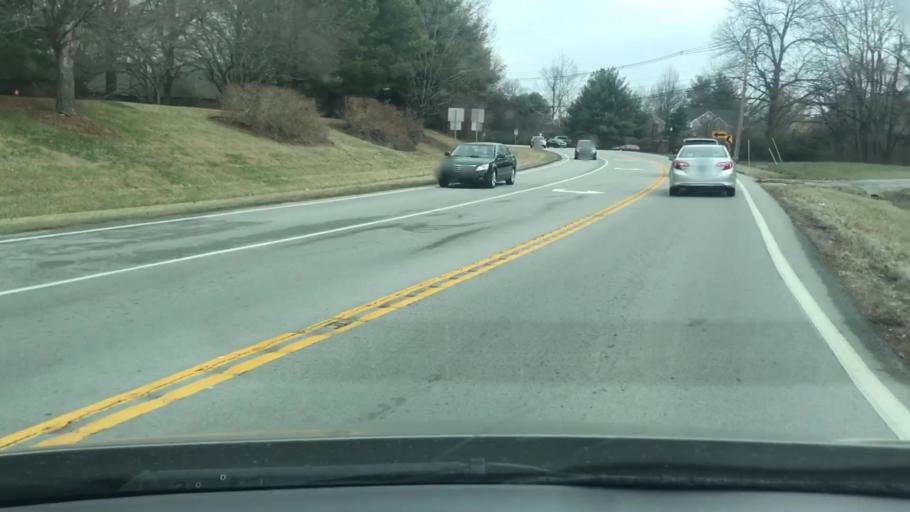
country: US
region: Kentucky
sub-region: Jefferson County
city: Graymoor-Devondale
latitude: 38.2884
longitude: -85.6208
